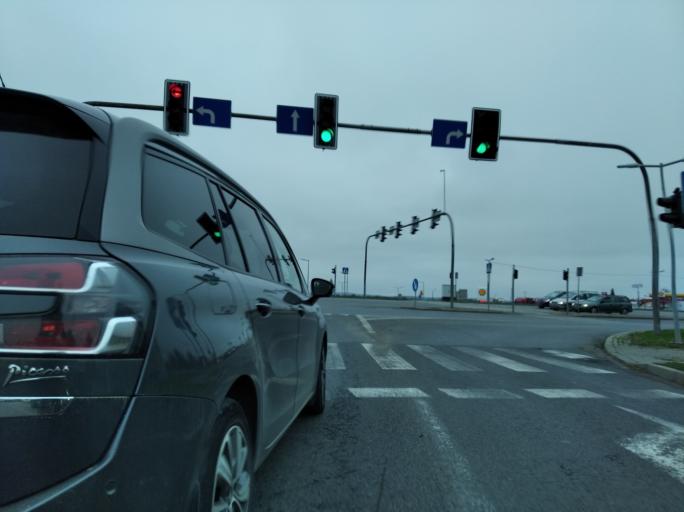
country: PL
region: Subcarpathian Voivodeship
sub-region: Krosno
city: Krosno
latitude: 49.6921
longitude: 21.7356
